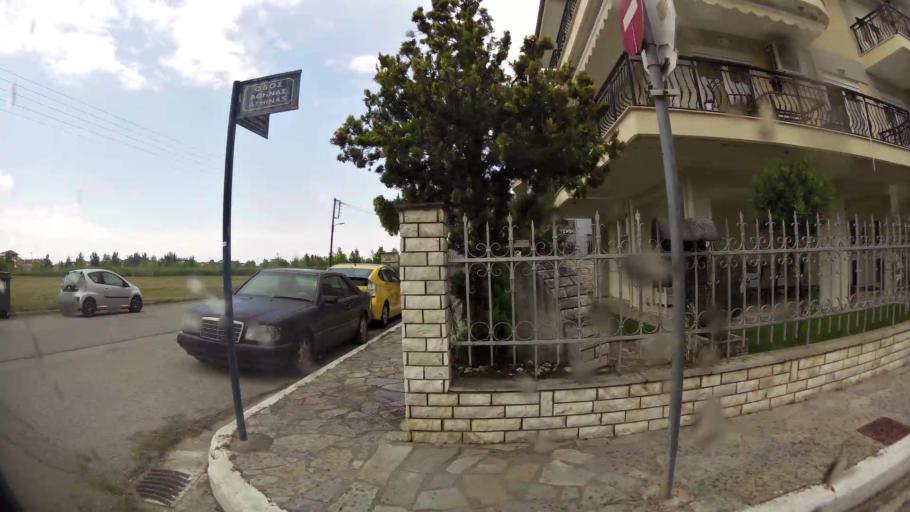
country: GR
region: Central Macedonia
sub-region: Nomos Pierias
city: Paralia
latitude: 40.2731
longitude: 22.5982
